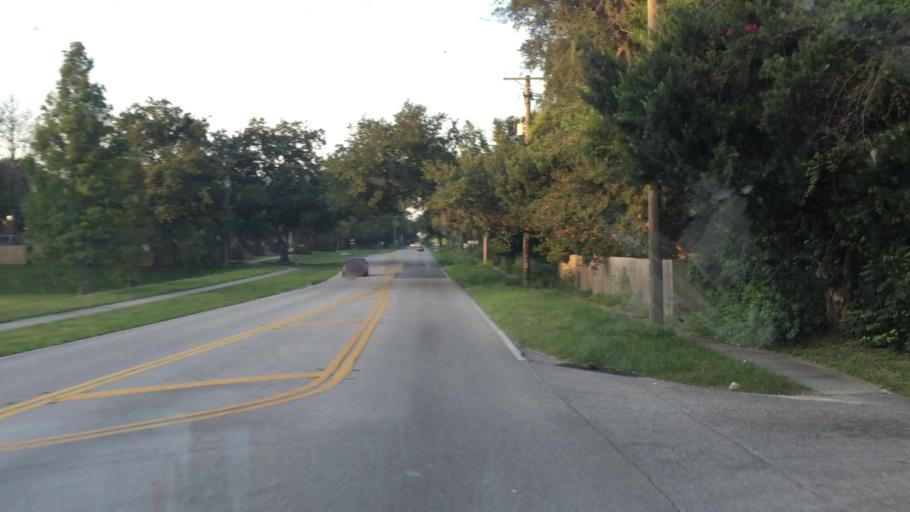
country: US
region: Florida
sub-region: Hillsborough County
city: Brandon
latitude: 27.9548
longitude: -82.2777
